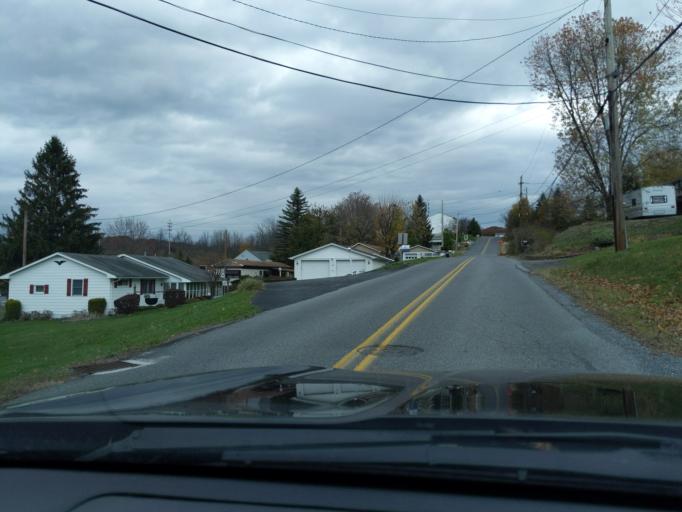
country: US
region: Pennsylvania
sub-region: Blair County
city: Greenwood
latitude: 40.5324
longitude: -78.3676
